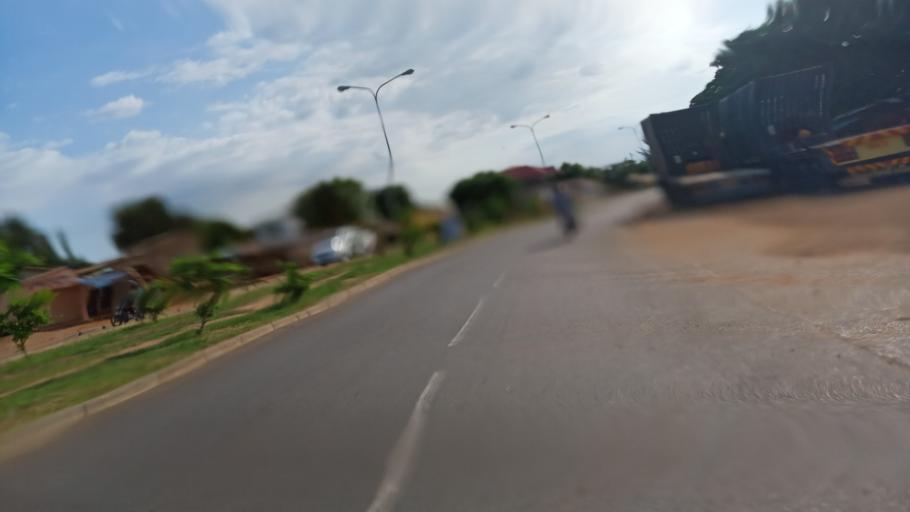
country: TG
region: Maritime
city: Lome
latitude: 6.1874
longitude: 1.2612
